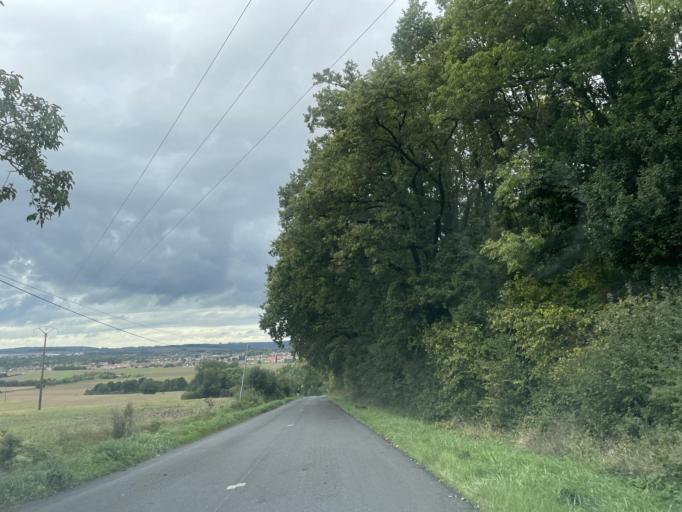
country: FR
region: Ile-de-France
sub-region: Departement de Seine-et-Marne
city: Trilport
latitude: 48.9399
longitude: 2.9626
